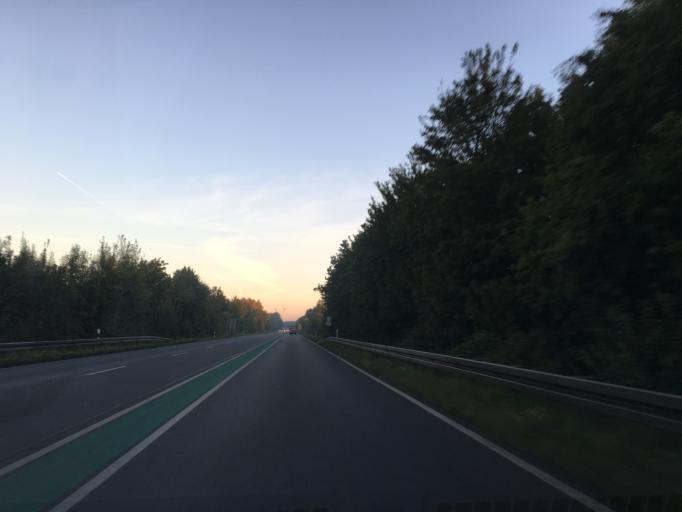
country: DE
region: North Rhine-Westphalia
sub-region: Regierungsbezirk Munster
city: Altenberge
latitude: 52.0590
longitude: 7.4393
